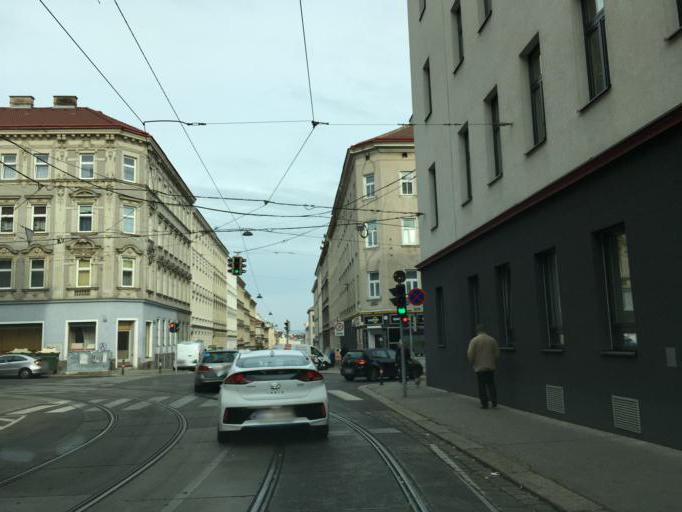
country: AT
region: Vienna
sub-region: Wien Stadt
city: Vienna
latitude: 48.2059
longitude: 16.3277
